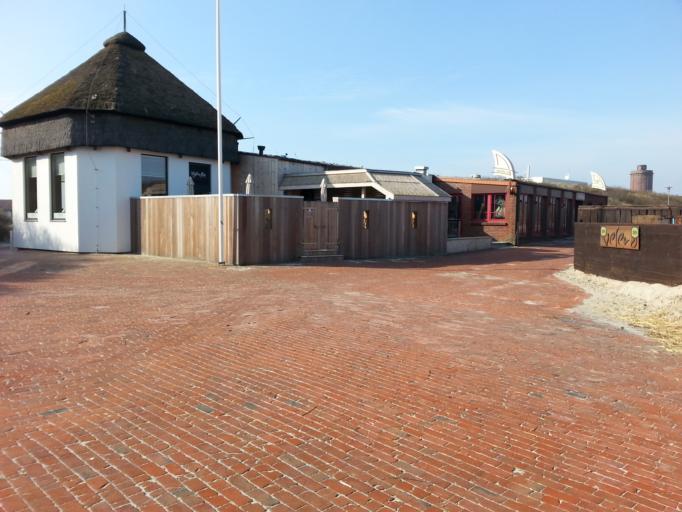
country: DE
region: Lower Saxony
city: Juist
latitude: 53.6808
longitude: 7.0017
